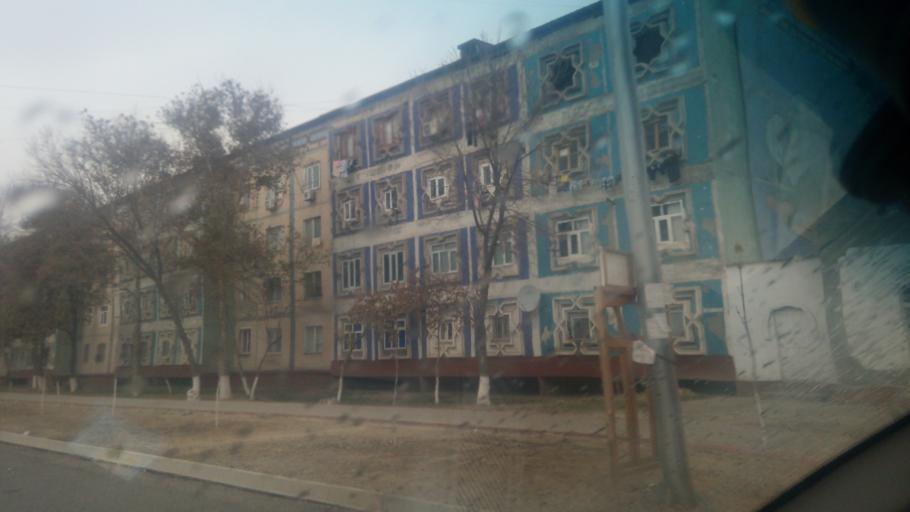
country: UZ
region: Sirdaryo
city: Guliston
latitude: 40.5029
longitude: 68.7750
